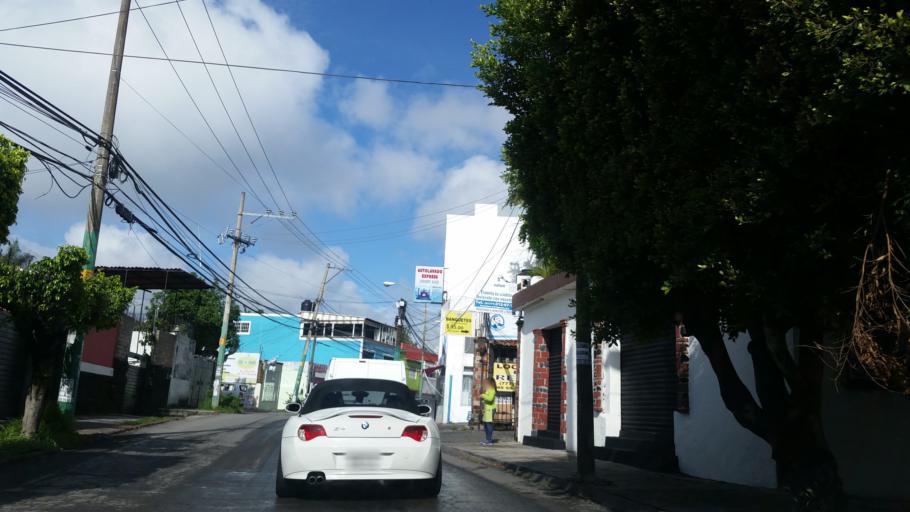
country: MX
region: Morelos
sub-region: Cuernavaca
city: Cuernavaca
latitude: 18.9208
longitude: -99.2170
